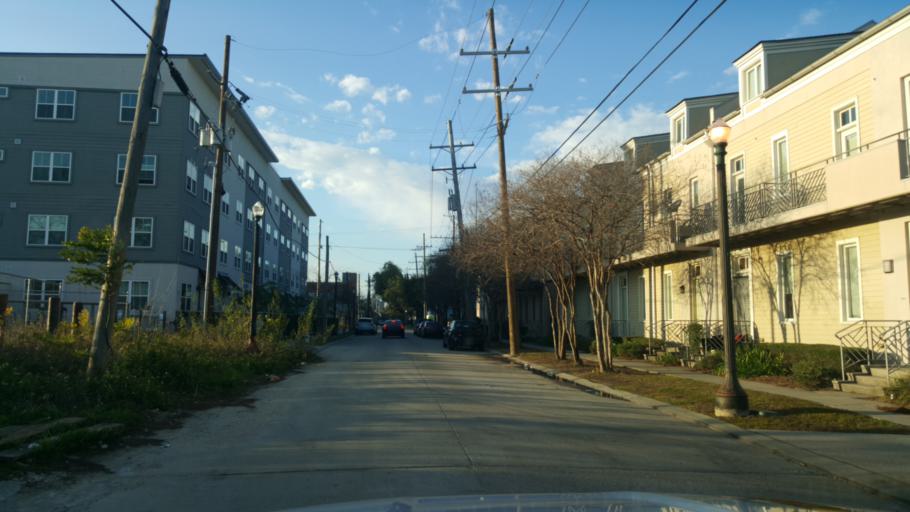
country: US
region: Louisiana
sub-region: Jefferson Parish
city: Gretna
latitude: 29.9255
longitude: -90.0717
